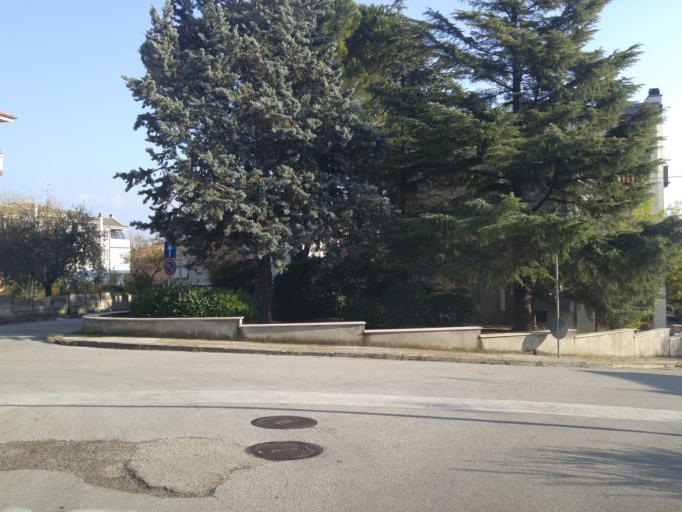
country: IT
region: The Marches
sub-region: Provincia di Pesaro e Urbino
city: Calcinelli
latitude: 43.7542
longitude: 12.9128
